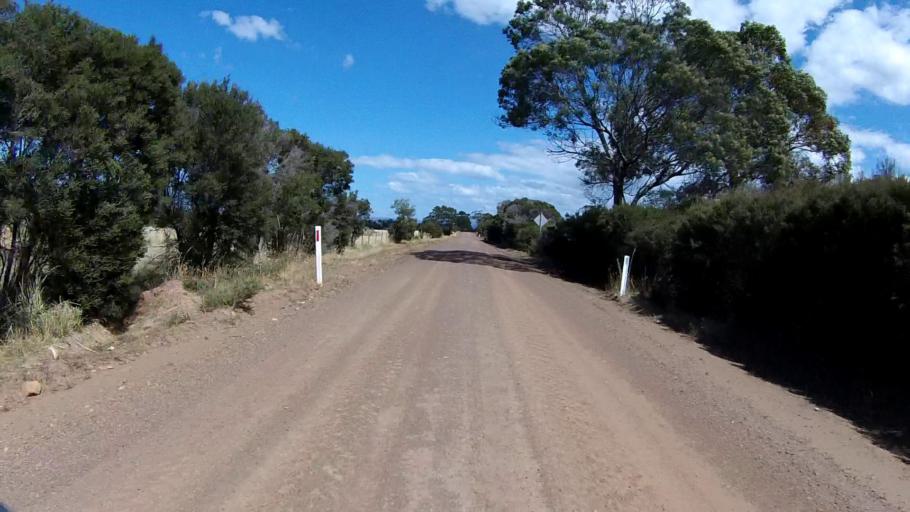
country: AU
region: Tasmania
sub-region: Break O'Day
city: St Helens
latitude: -41.9741
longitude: 148.0723
